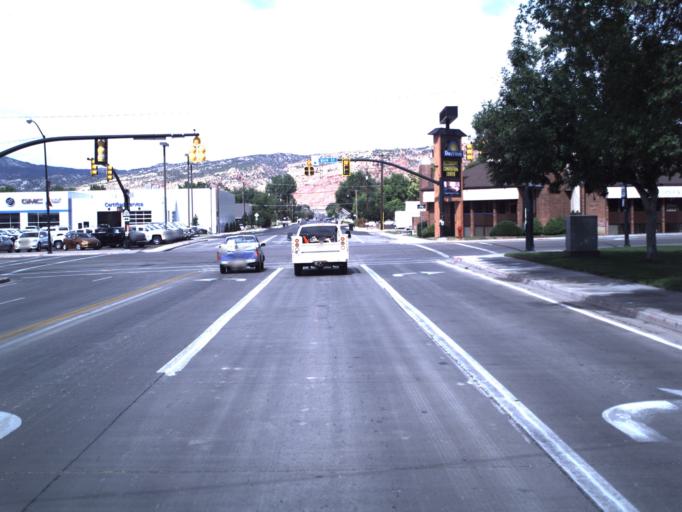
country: US
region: Utah
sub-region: Sevier County
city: Richfield
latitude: 38.7723
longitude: -112.0841
